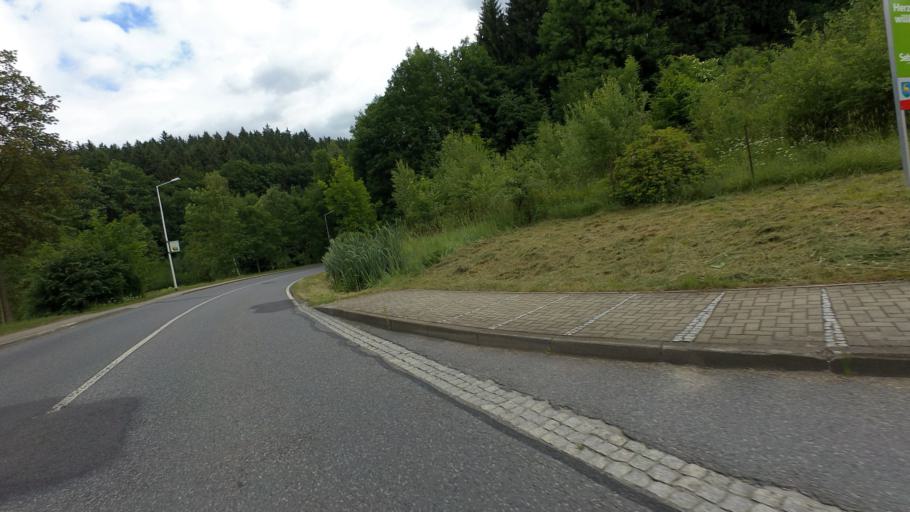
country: DE
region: Saxony
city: Sebnitz
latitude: 50.9827
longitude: 14.2623
